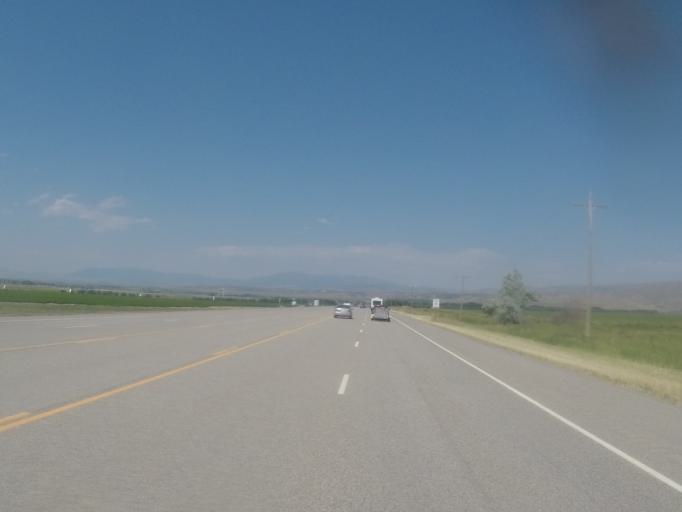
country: US
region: Montana
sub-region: Broadwater County
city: Townsend
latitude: 46.1426
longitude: -111.4754
